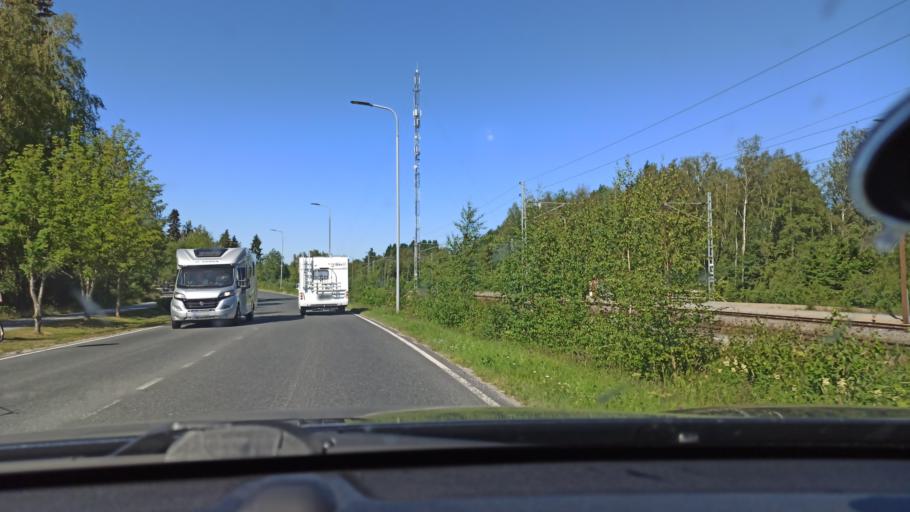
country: FI
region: Ostrobothnia
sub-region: Jakobstadsregionen
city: Jakobstad
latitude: 63.6701
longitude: 22.7148
